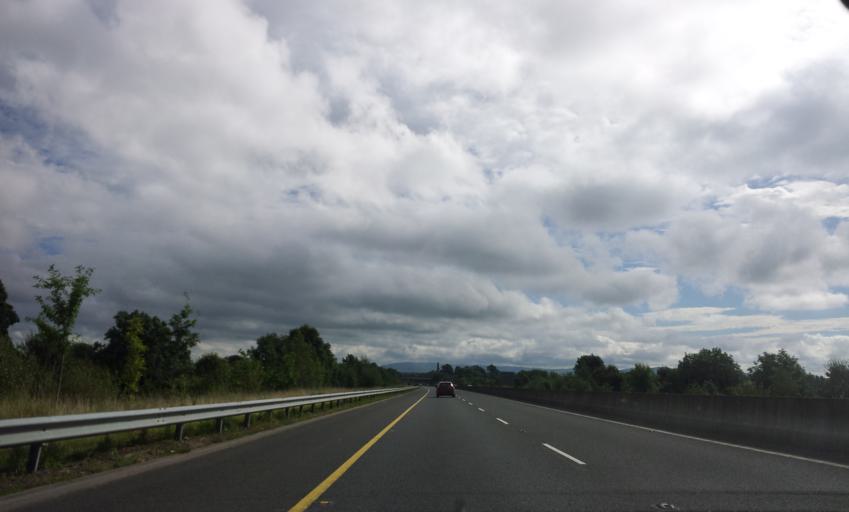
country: IE
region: Munster
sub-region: North Tipperary
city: Nenagh
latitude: 52.8445
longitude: -8.2183
